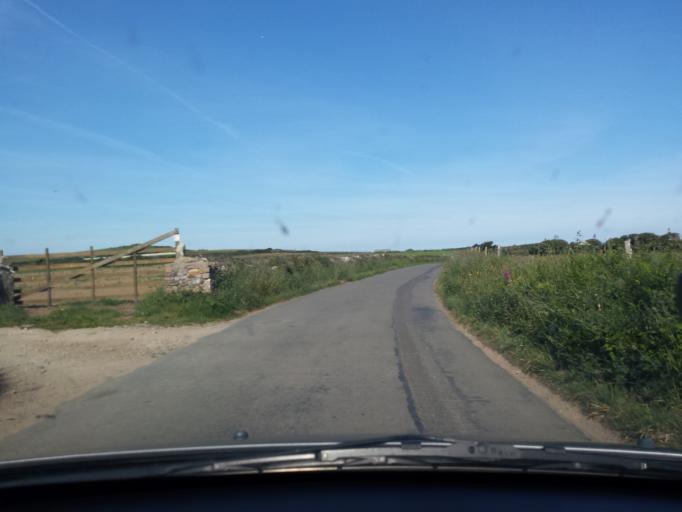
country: FR
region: Lower Normandy
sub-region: Departement de la Manche
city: Beaumont-Hague
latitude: 49.6761
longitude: -1.9315
